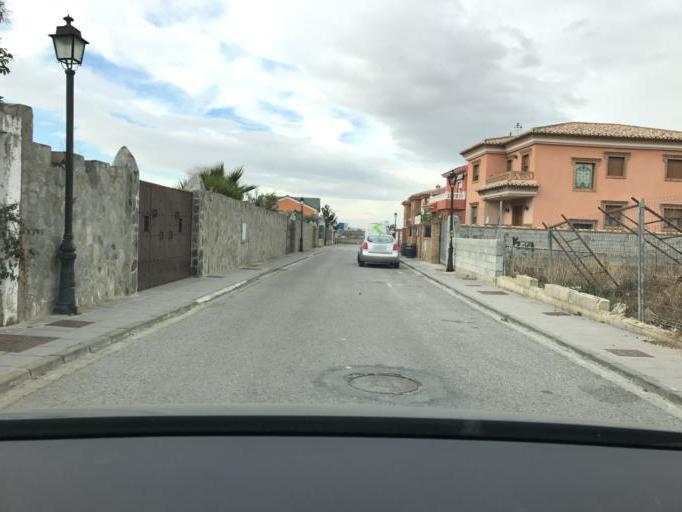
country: ES
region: Andalusia
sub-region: Provincia de Granada
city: Ogijares
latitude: 37.1248
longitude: -3.6105
